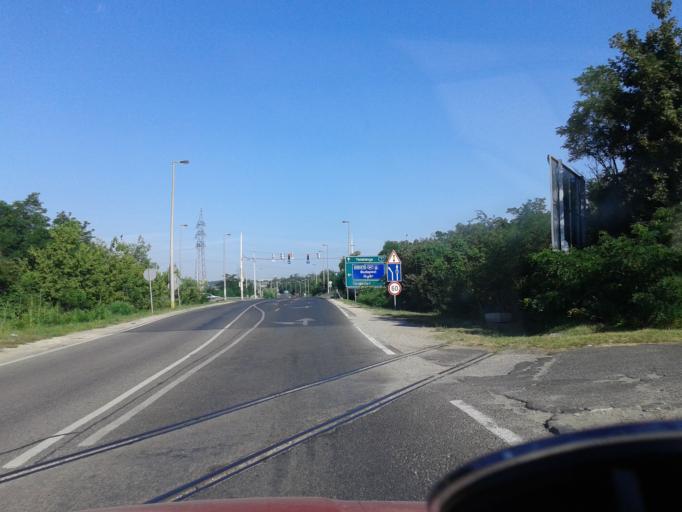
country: HU
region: Pest
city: Toeroekbalint
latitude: 47.4589
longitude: 18.9042
